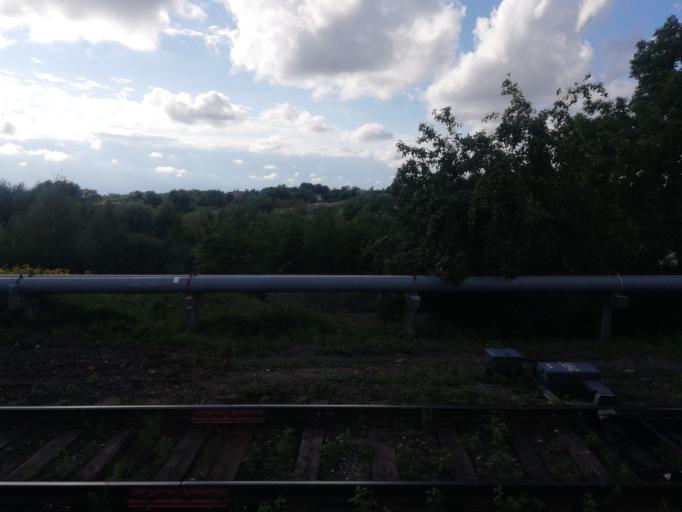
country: RU
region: Kaliningrad
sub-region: Gorod Kaliningrad
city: Kaliningrad
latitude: 54.6883
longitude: 20.4784
